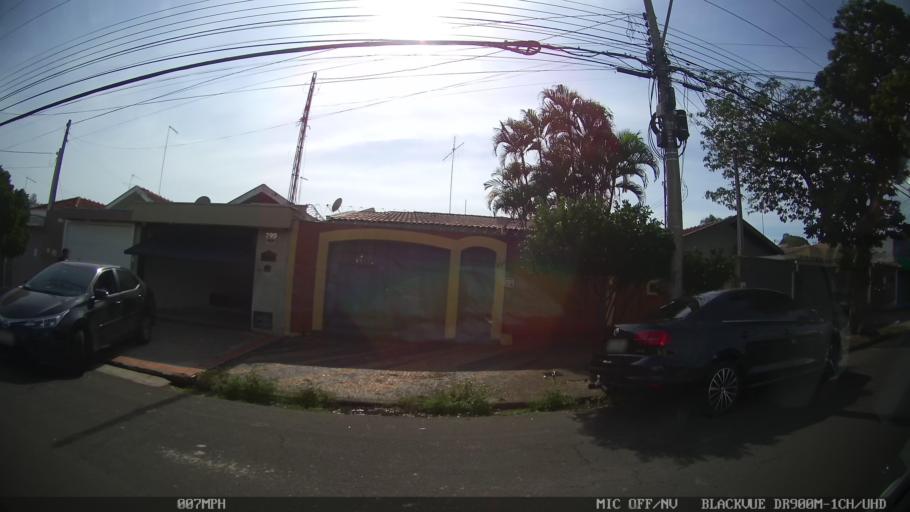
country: BR
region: Sao Paulo
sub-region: Piracicaba
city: Piracicaba
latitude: -22.7111
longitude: -47.6592
